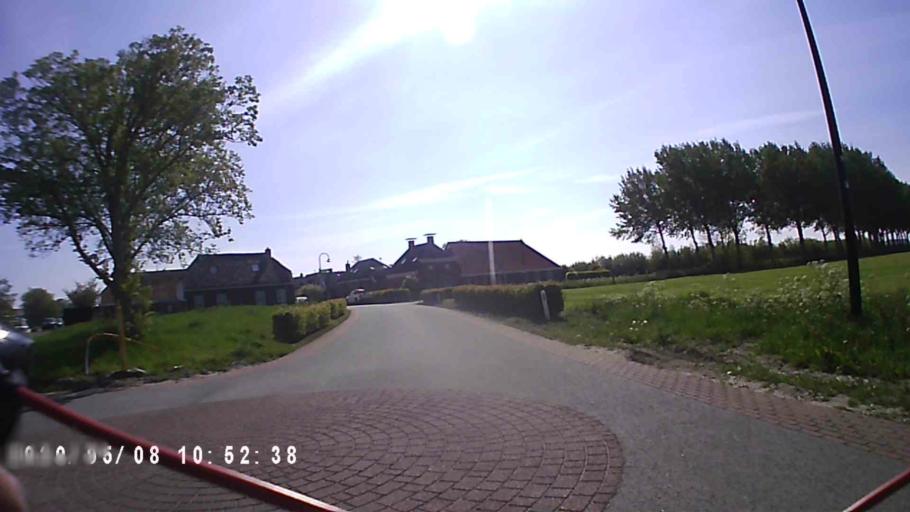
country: NL
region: Groningen
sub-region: Gemeente Bedum
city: Bedum
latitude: 53.3350
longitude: 6.5815
